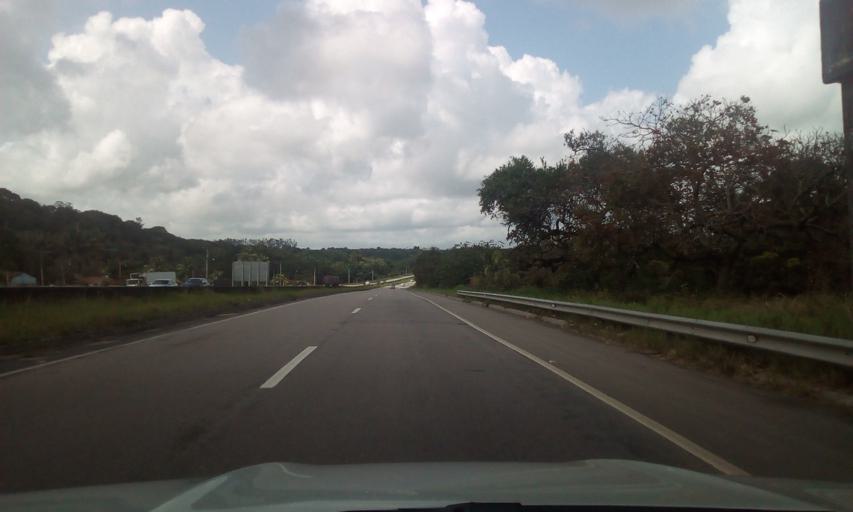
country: BR
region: Paraiba
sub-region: Alhandra
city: Alhandra
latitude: -7.4005
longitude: -34.9553
